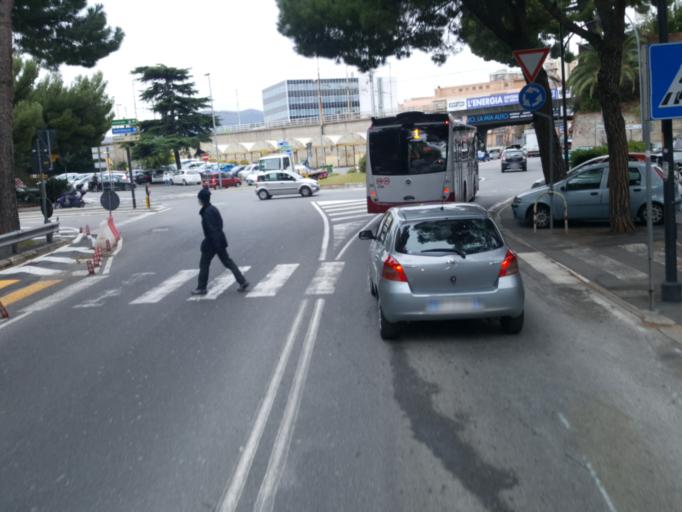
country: IT
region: Liguria
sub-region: Provincia di Savona
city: Savona
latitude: 44.3026
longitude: 8.4707
